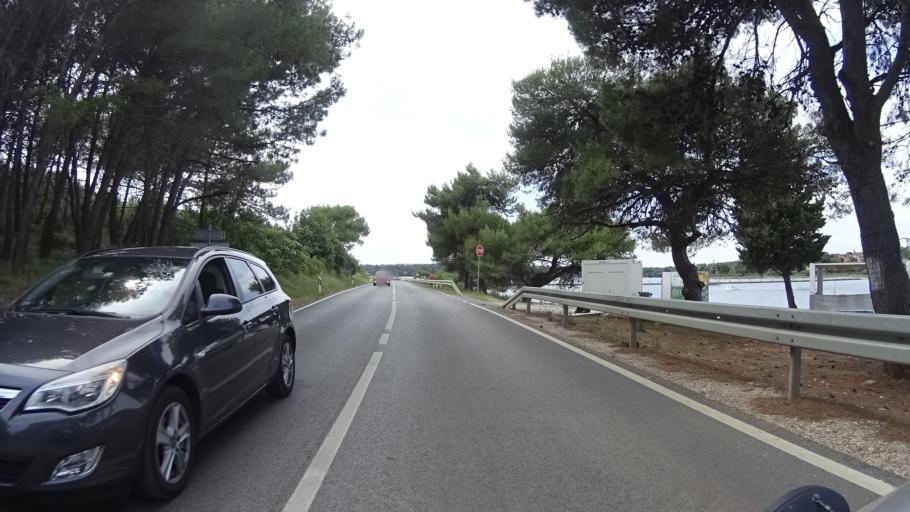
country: HR
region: Istarska
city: Medulin
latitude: 44.8164
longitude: 13.8981
